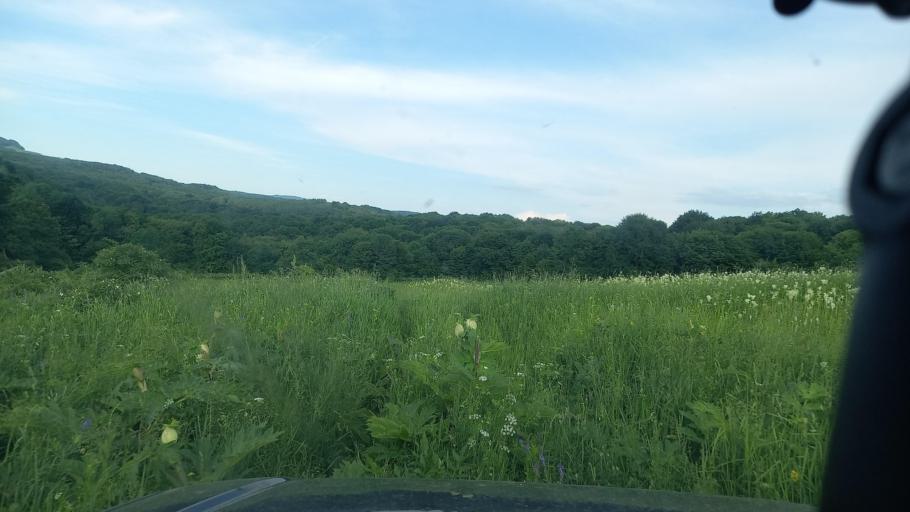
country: RU
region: Karachayevo-Cherkesiya
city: Kurdzhinovo
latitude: 44.1321
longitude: 41.0958
